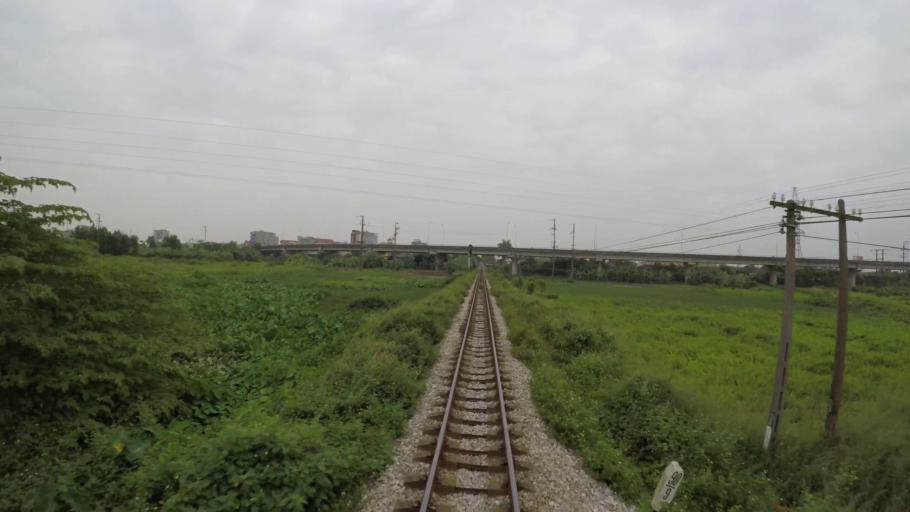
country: VN
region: Hai Phong
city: An Duong
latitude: 20.9096
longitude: 106.5712
